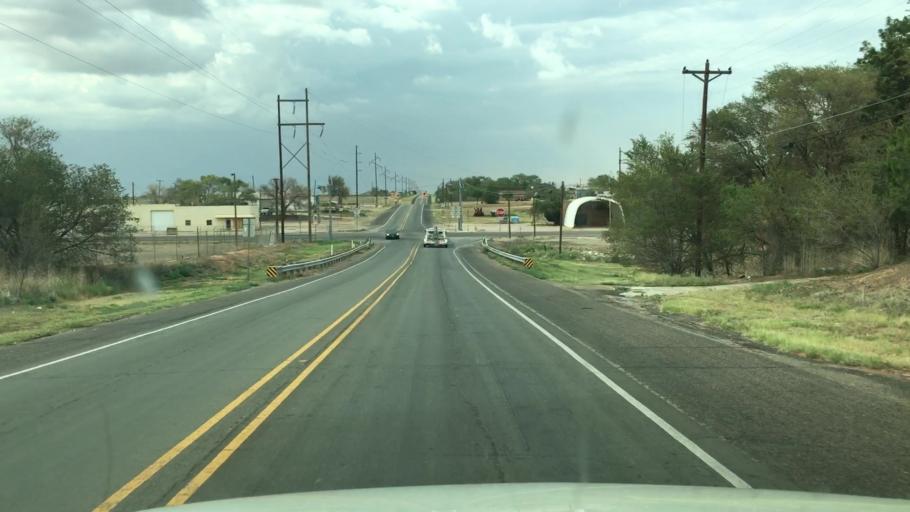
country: US
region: Texas
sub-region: Terry County
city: Brownfield
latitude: 33.1779
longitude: -102.2915
